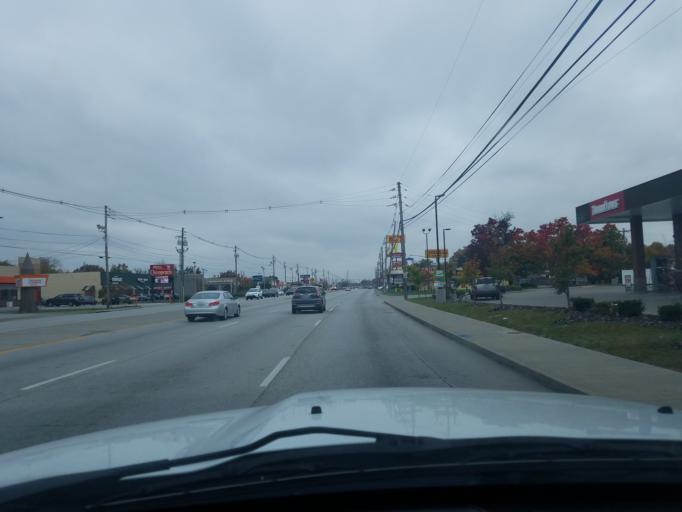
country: US
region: Kentucky
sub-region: Jefferson County
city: Shively
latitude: 38.1784
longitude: -85.8189
